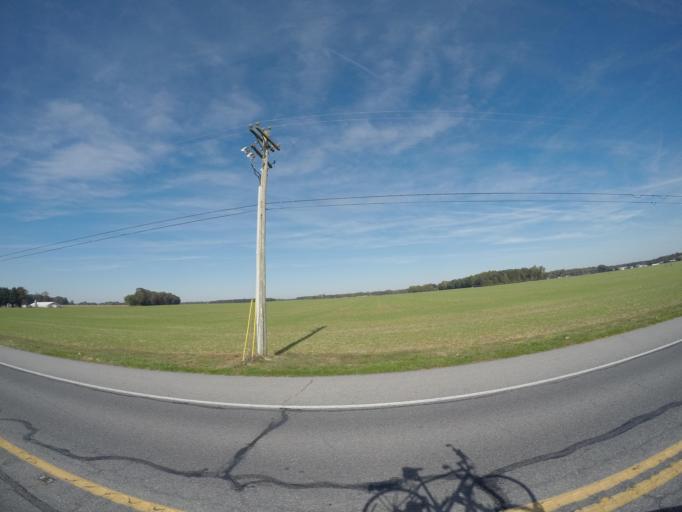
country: US
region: Delaware
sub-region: Sussex County
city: Milton
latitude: 38.7910
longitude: -75.2948
